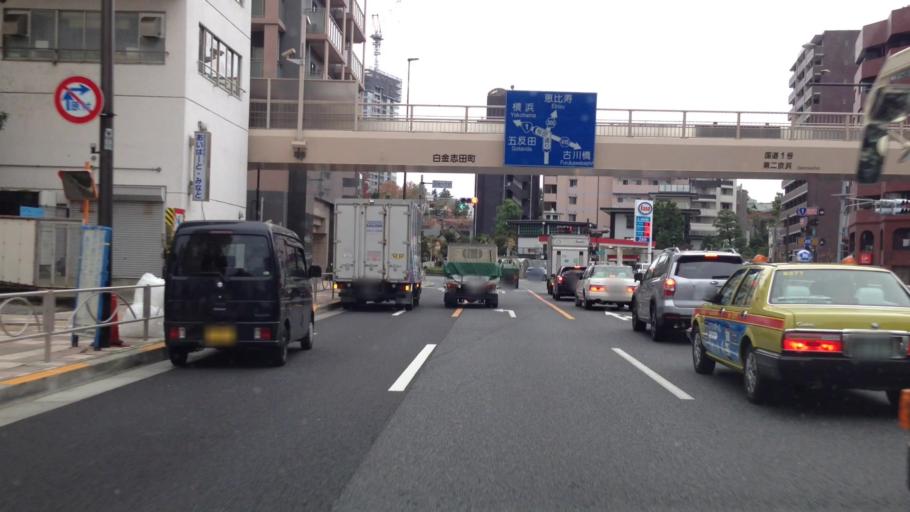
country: JP
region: Tokyo
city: Tokyo
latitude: 35.6433
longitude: 139.7351
